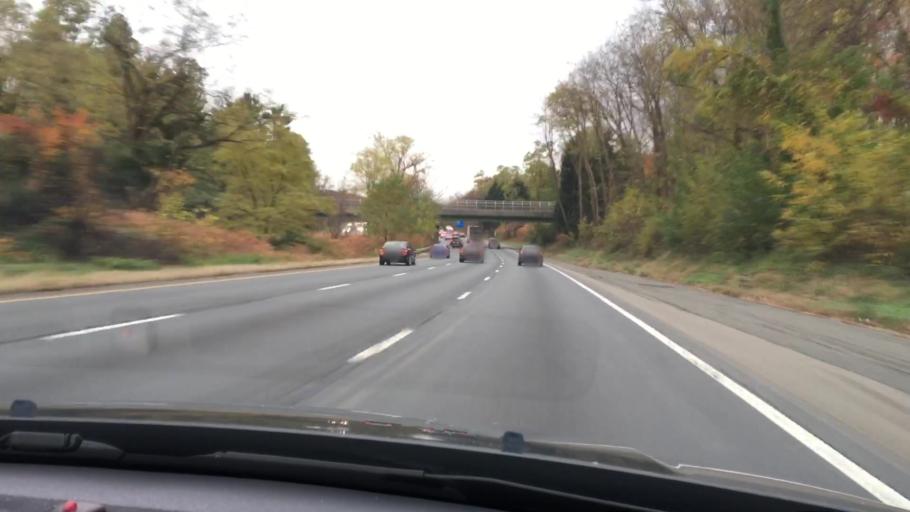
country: US
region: New Jersey
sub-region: Somerset County
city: Bernardsville
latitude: 40.7555
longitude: -74.5246
